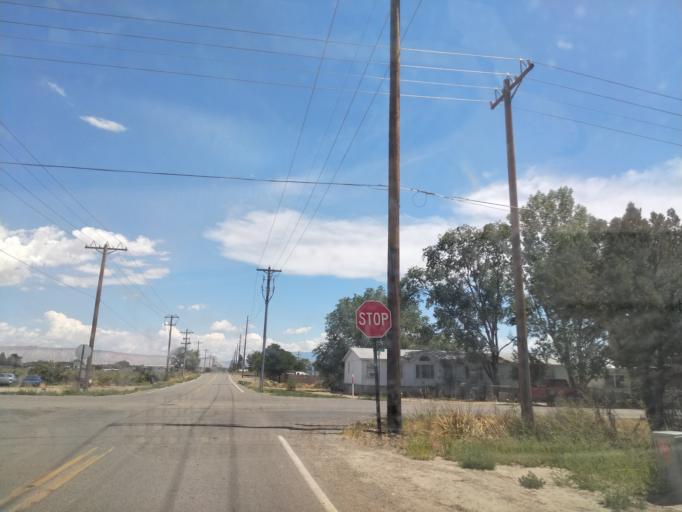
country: US
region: Colorado
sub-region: Mesa County
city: Redlands
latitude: 39.1208
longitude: -108.6549
